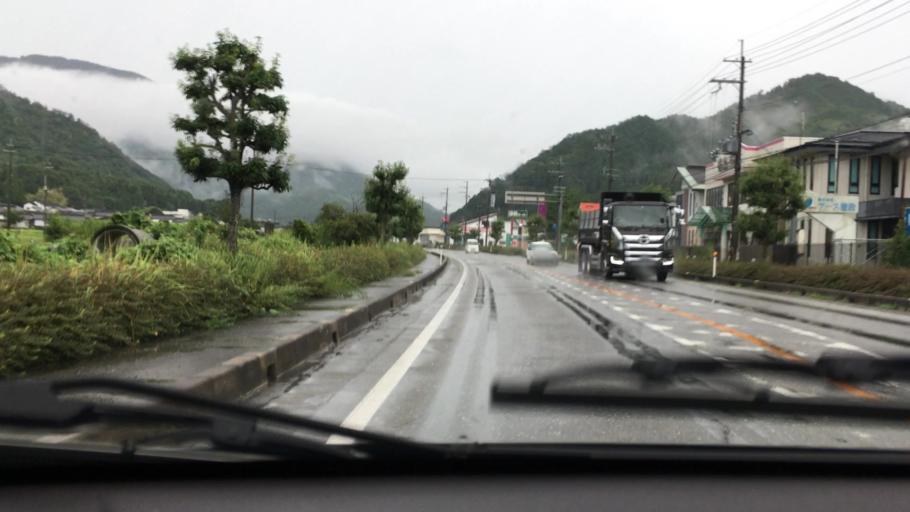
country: JP
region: Hyogo
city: Toyooka
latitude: 35.3114
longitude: 134.8410
